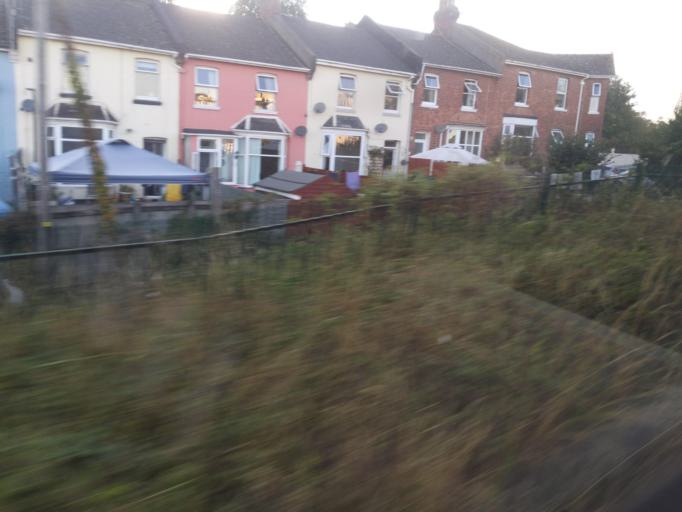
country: GB
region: England
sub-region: Borough of Torbay
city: Torquay
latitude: 50.4711
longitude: -3.5453
